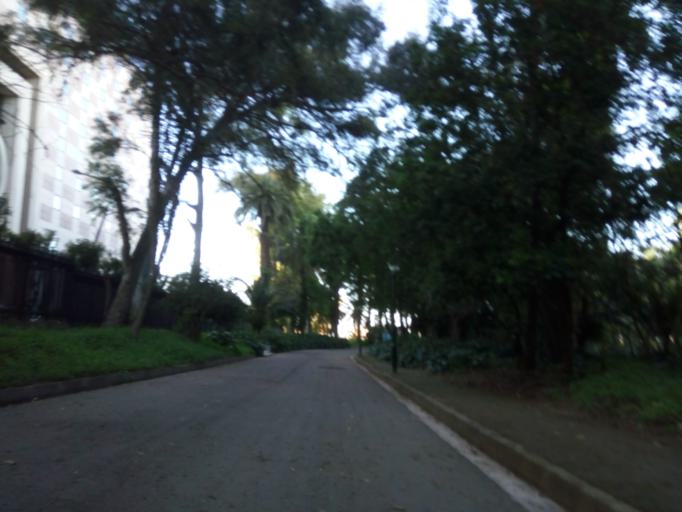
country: DZ
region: Alger
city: Algiers
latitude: 36.7505
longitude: 3.0736
